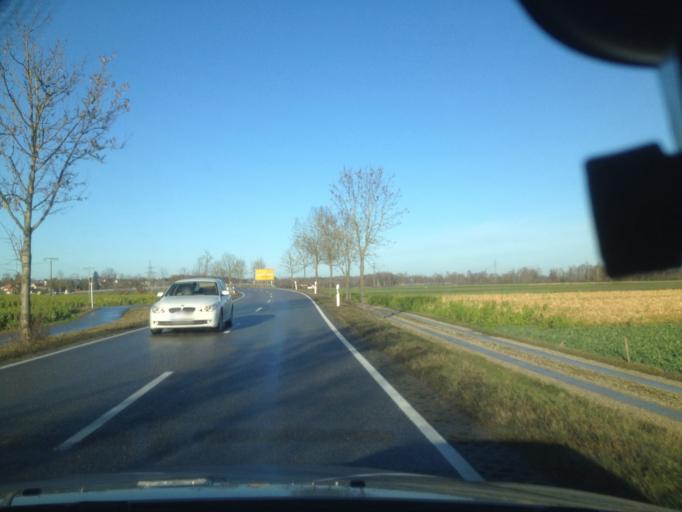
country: DE
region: Bavaria
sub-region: Swabia
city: Burgau
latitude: 48.4482
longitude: 10.3913
